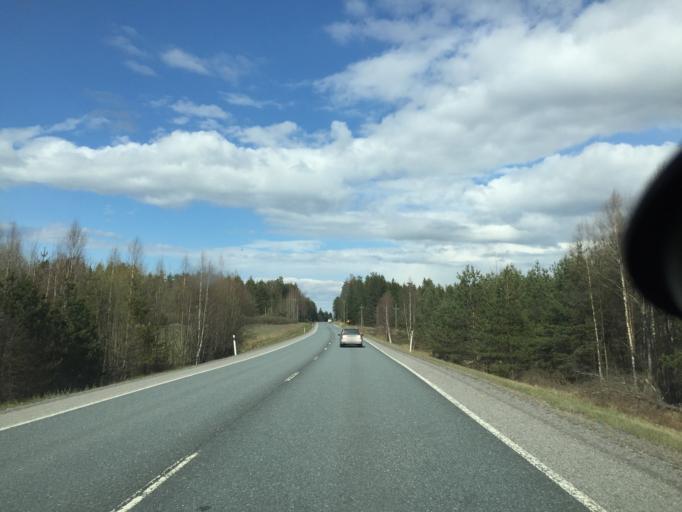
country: FI
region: Uusimaa
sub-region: Raaseporin
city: Inga
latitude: 60.1400
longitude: 23.8856
